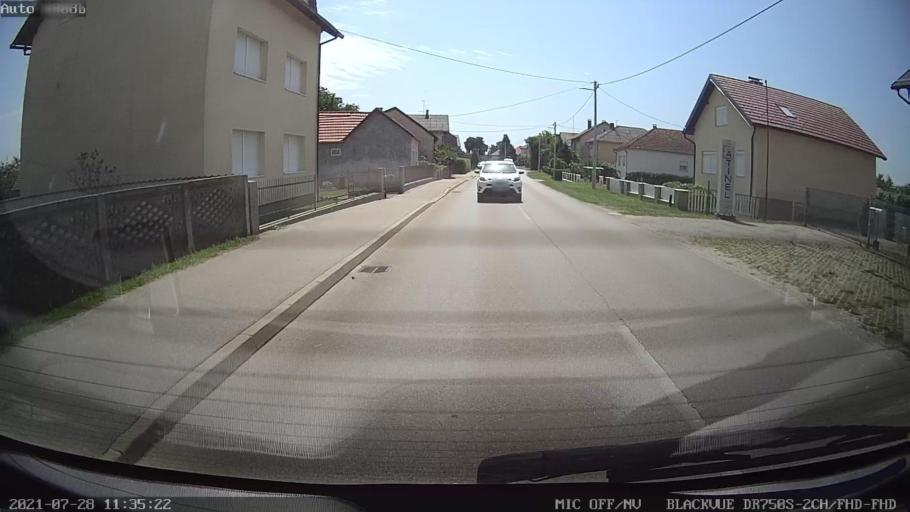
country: HR
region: Varazdinska
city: Varazdin
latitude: 46.2959
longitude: 16.3702
